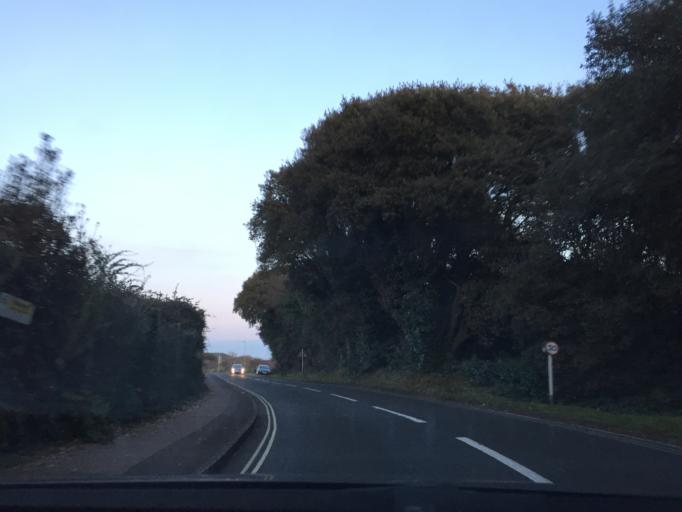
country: GB
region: England
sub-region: Hampshire
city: Gosport
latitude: 50.7785
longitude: -1.1390
